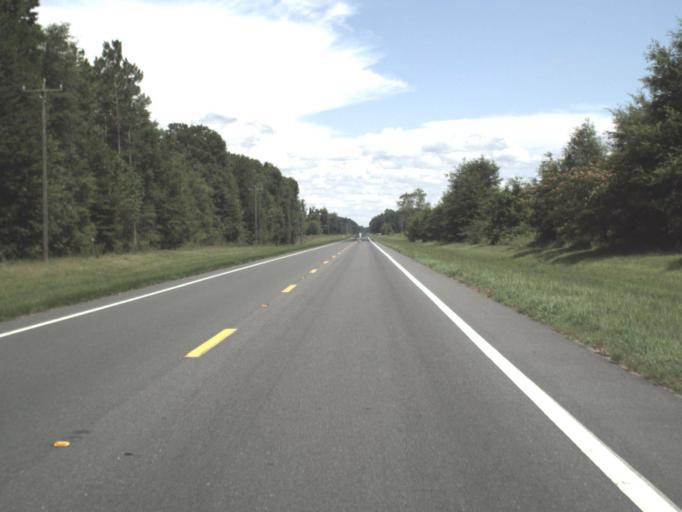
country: US
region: Florida
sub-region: Lafayette County
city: Mayo
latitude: 30.0775
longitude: -83.2117
